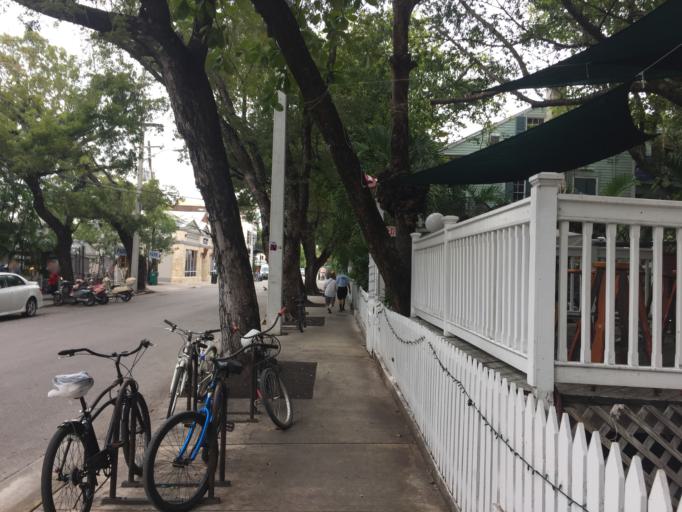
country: US
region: Florida
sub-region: Monroe County
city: Key West
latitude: 24.5574
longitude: -81.8054
